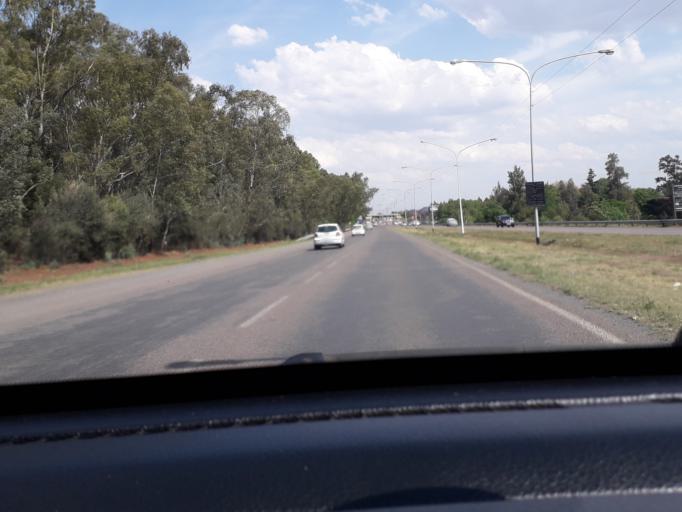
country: ZA
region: Gauteng
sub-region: City of Tshwane Metropolitan Municipality
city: Centurion
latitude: -25.8524
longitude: 28.2174
